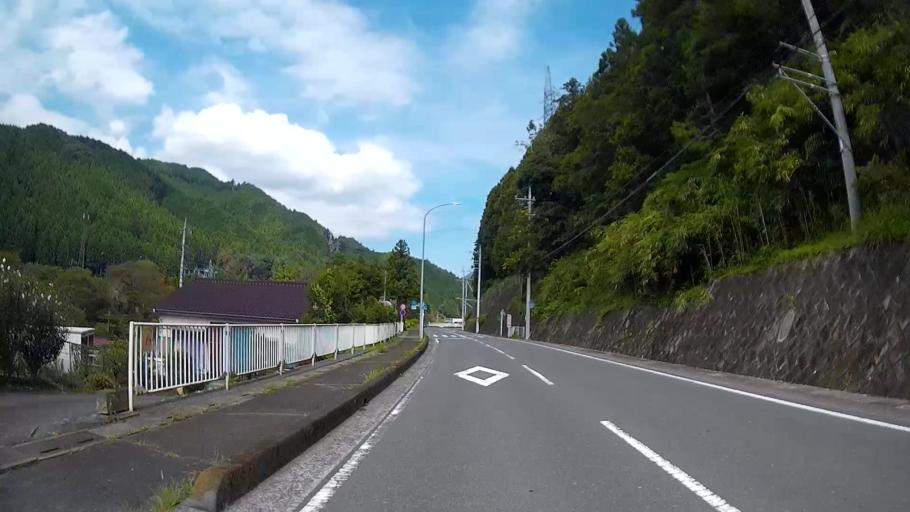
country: JP
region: Tokyo
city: Ome
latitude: 35.8876
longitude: 139.1812
